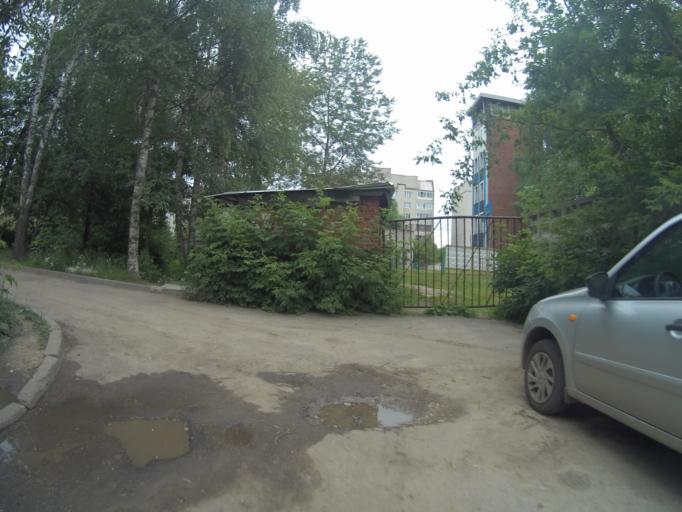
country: RU
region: Vladimir
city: Vladimir
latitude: 56.1238
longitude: 40.3714
